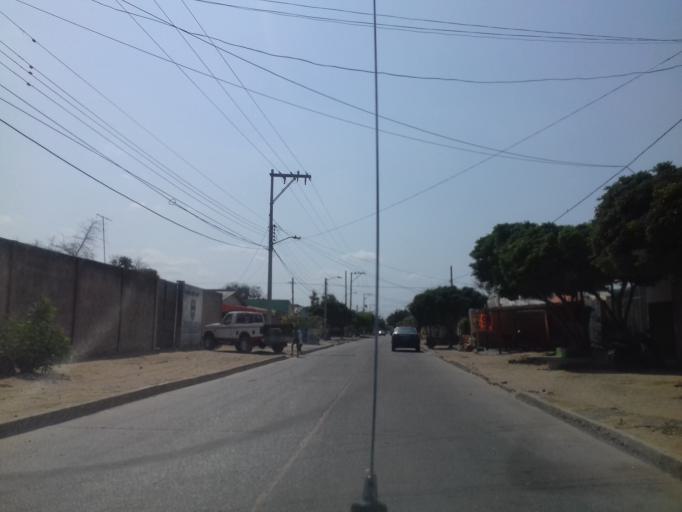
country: CO
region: La Guajira
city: Maicao
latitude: 11.3822
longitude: -72.2463
